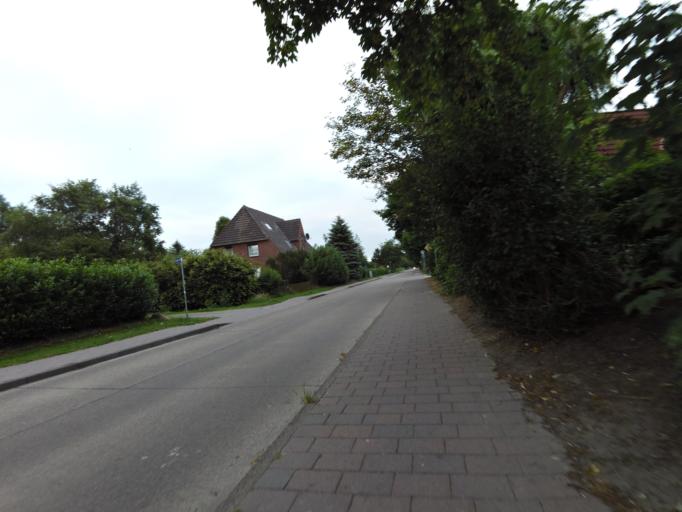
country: DE
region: Lower Saxony
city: Padingbuttel
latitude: 53.7335
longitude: 8.5243
